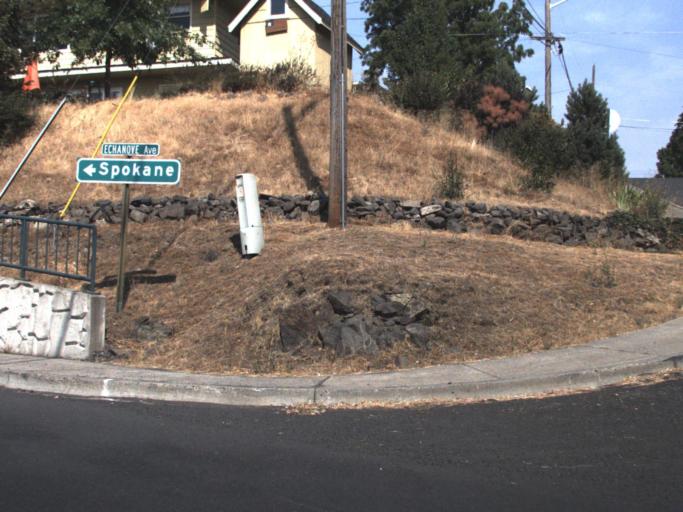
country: US
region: Idaho
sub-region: Latah County
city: Moscow
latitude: 46.9109
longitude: -117.0773
